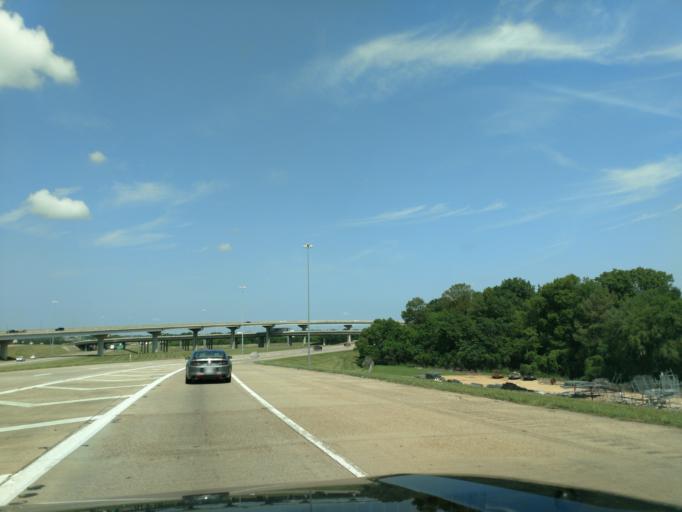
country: US
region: Mississippi
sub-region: Hinds County
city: Jackson
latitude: 32.2762
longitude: -90.1702
